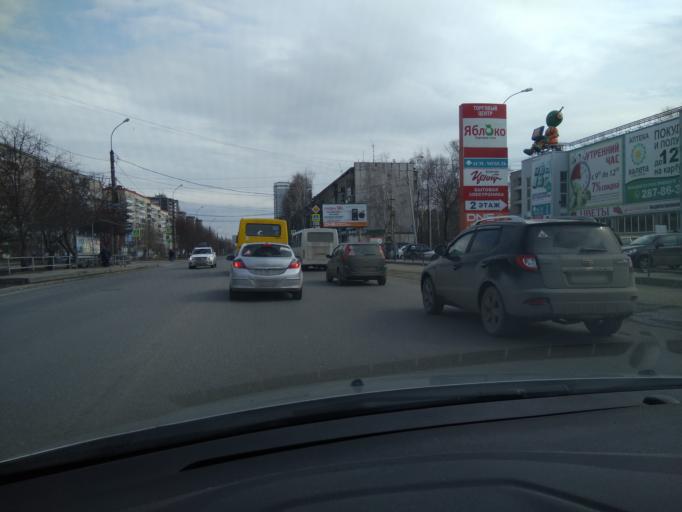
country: RU
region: Sverdlovsk
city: Shuvakish
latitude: 56.8660
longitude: 60.5325
